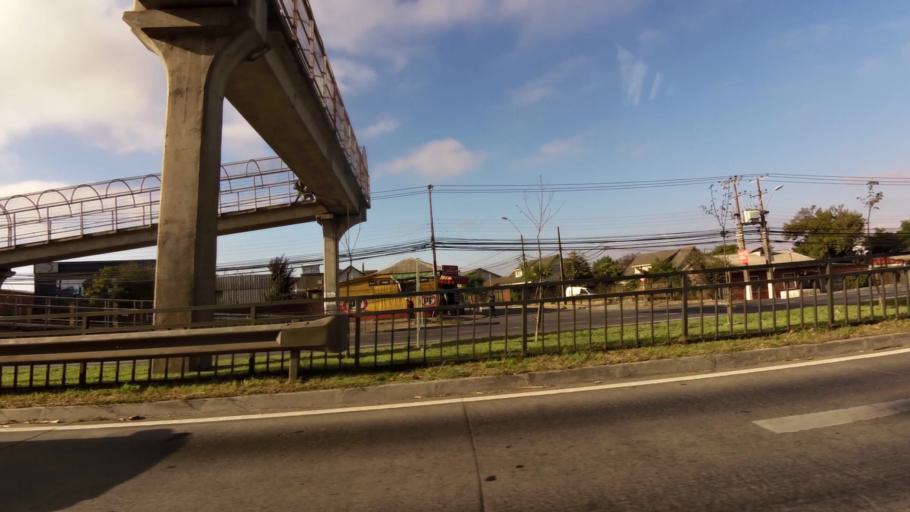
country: CL
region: Biobio
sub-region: Provincia de Concepcion
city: Concepcion
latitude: -36.7840
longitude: -73.0823
